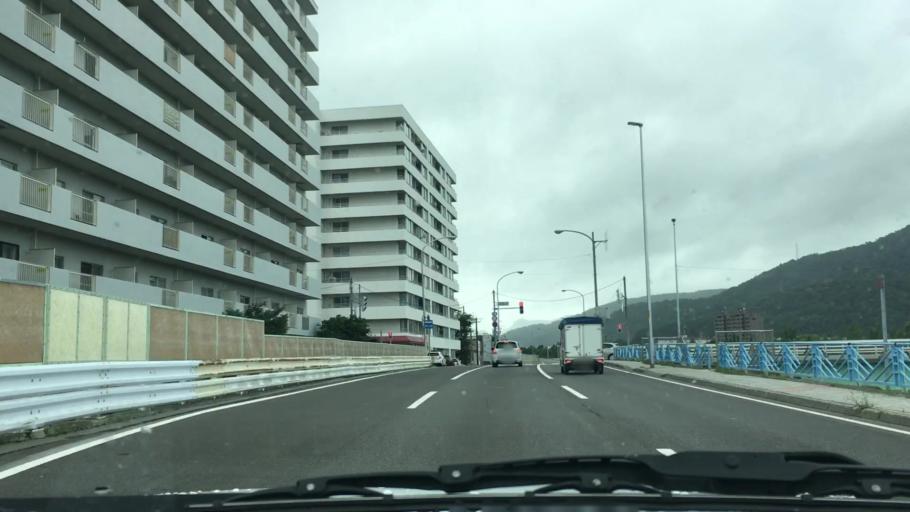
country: JP
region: Hokkaido
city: Sapporo
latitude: 43.0295
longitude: 141.3567
